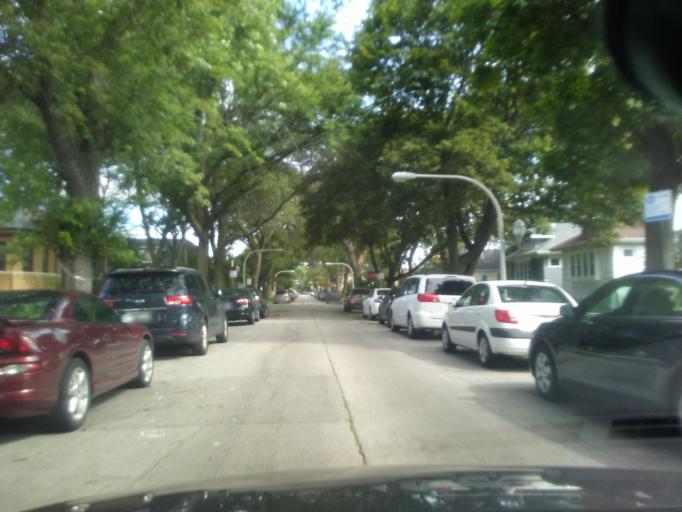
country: US
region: Illinois
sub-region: Cook County
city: Lincolnwood
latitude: 41.9953
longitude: -87.6935
